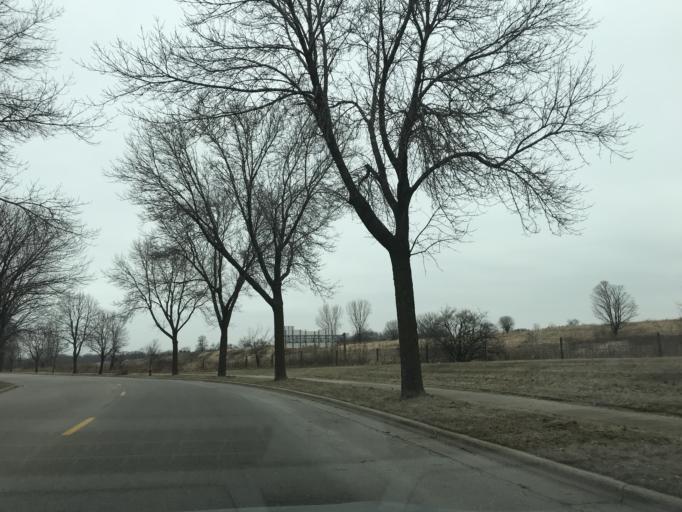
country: US
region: Wisconsin
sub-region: Dane County
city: Monona
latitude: 43.1010
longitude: -89.2893
